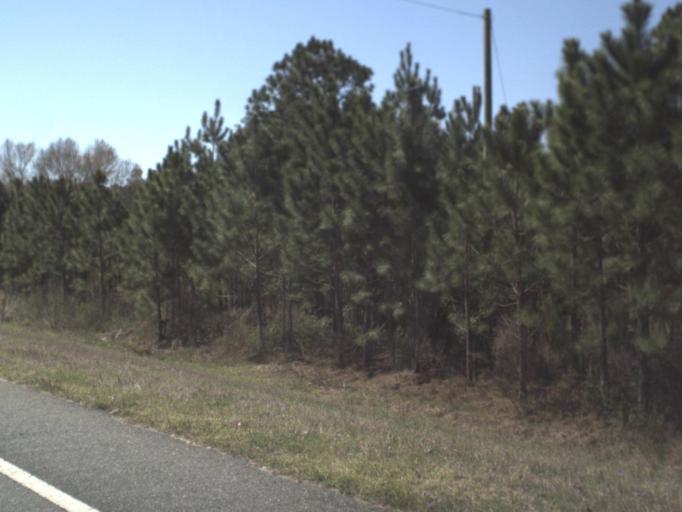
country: US
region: Florida
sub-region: Leon County
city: Woodville
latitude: 30.3458
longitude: -84.3104
